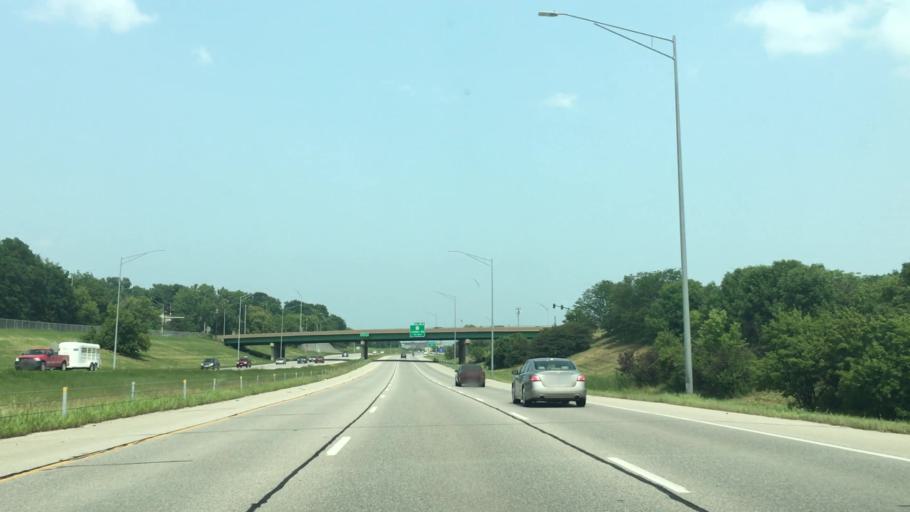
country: US
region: Iowa
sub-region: Linn County
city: Cedar Rapids
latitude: 42.0094
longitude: -91.6660
